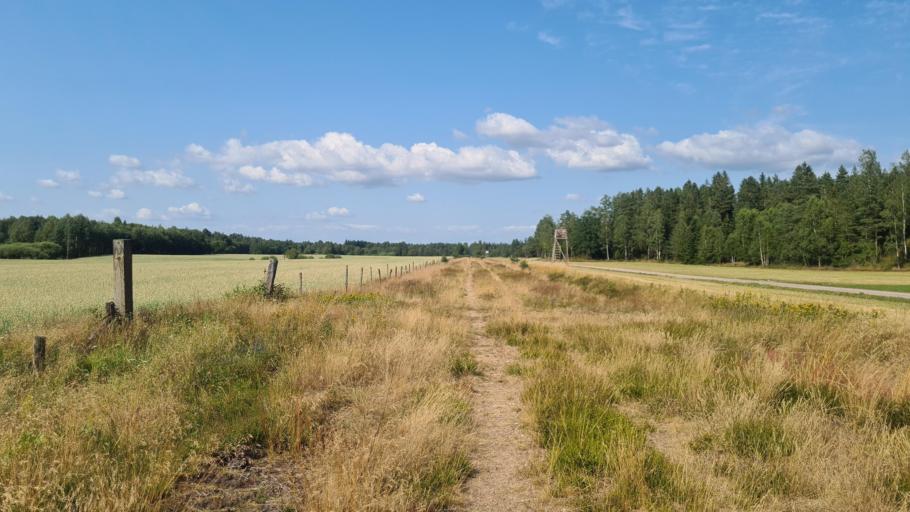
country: SE
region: Kronoberg
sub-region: Ljungby Kommun
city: Ljungby
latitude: 56.7528
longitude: 13.8844
